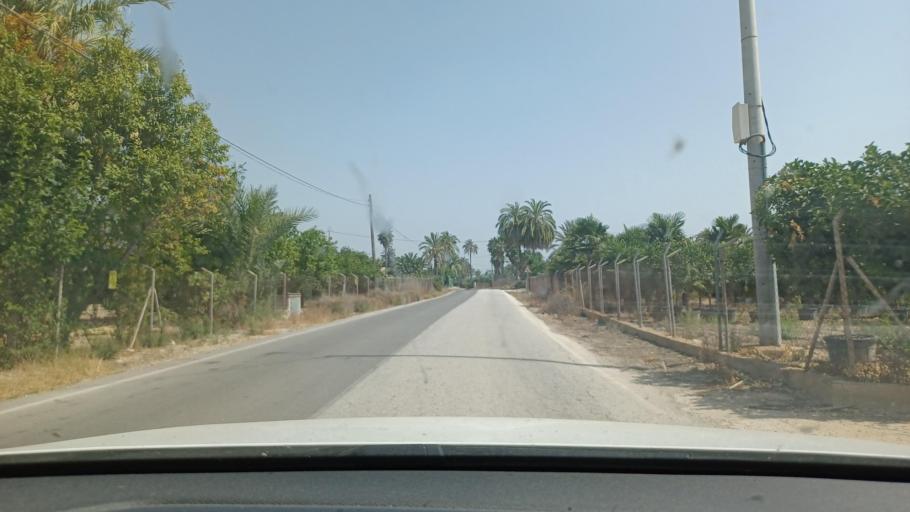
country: ES
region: Valencia
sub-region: Provincia de Alicante
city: Elche
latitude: 38.2349
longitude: -0.6931
